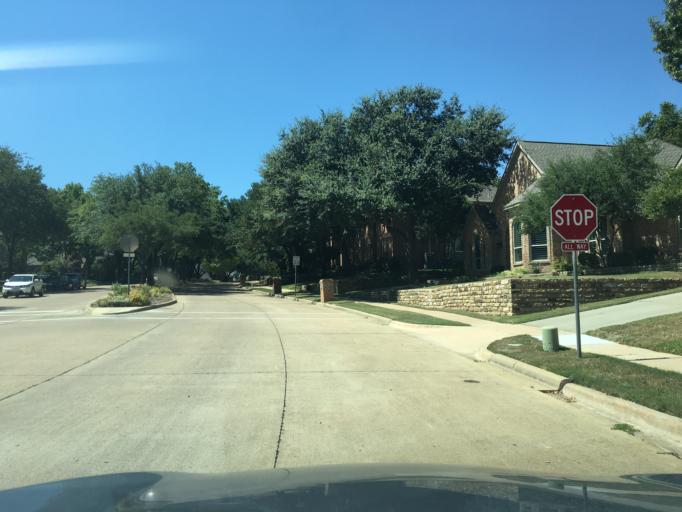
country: US
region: Texas
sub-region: Dallas County
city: Sachse
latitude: 32.9699
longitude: -96.6324
